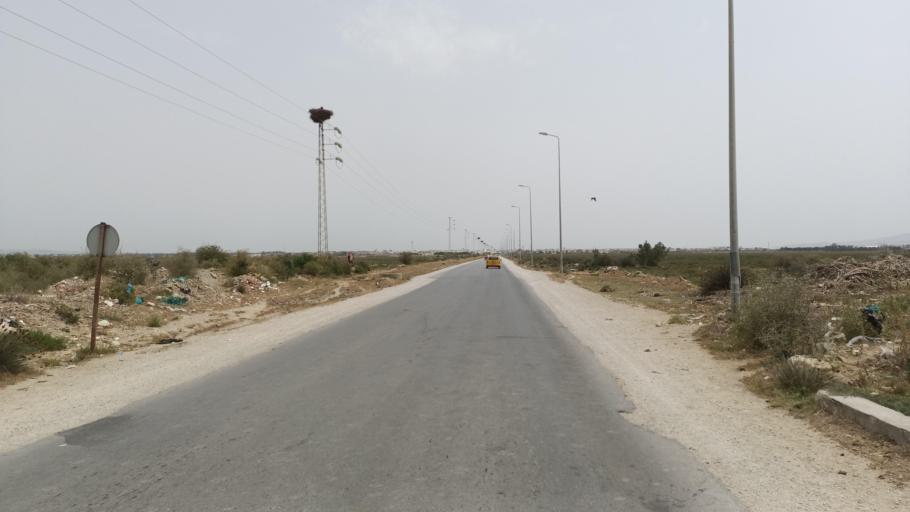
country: TN
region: Nabul
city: Manzil Bu Zalafah
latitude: 36.7228
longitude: 10.4727
